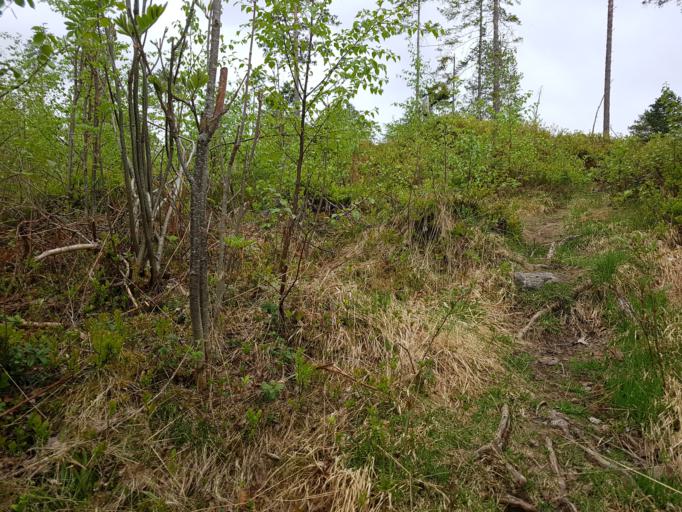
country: NO
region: Nord-Trondelag
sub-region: Levanger
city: Skogn
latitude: 63.6334
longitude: 11.2511
